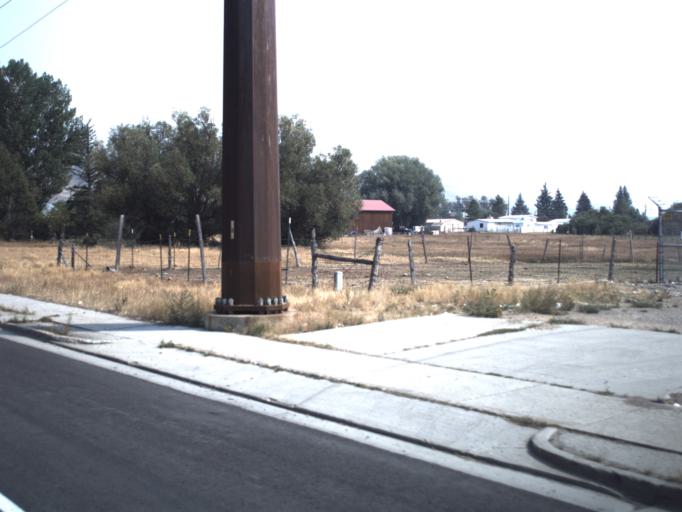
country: US
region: Utah
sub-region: Summit County
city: Kamas
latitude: 40.6399
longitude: -111.2833
